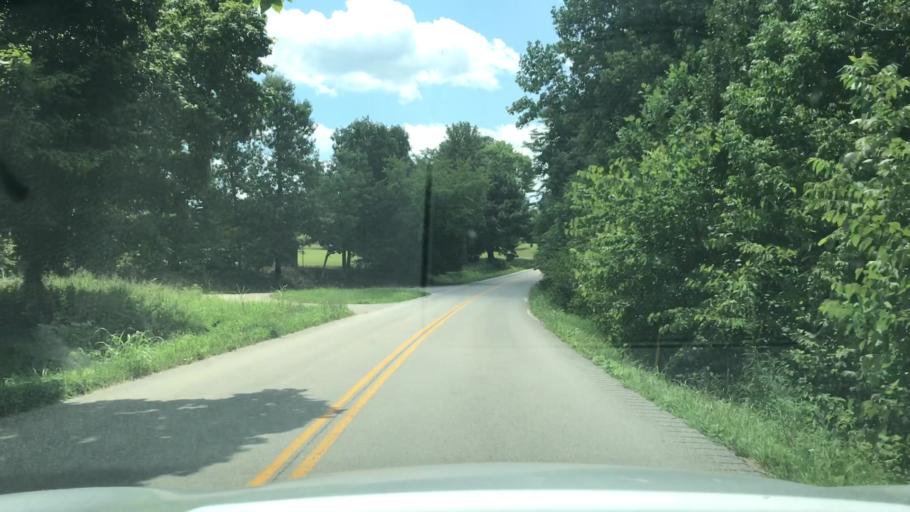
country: US
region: Kentucky
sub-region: Hopkins County
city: Nortonville
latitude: 37.1158
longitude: -87.3251
